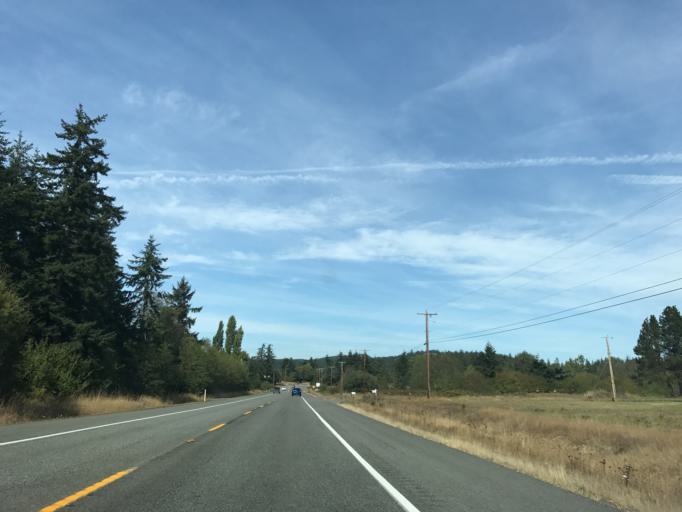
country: US
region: Washington
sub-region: Island County
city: Ault Field
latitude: 48.3816
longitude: -122.6504
